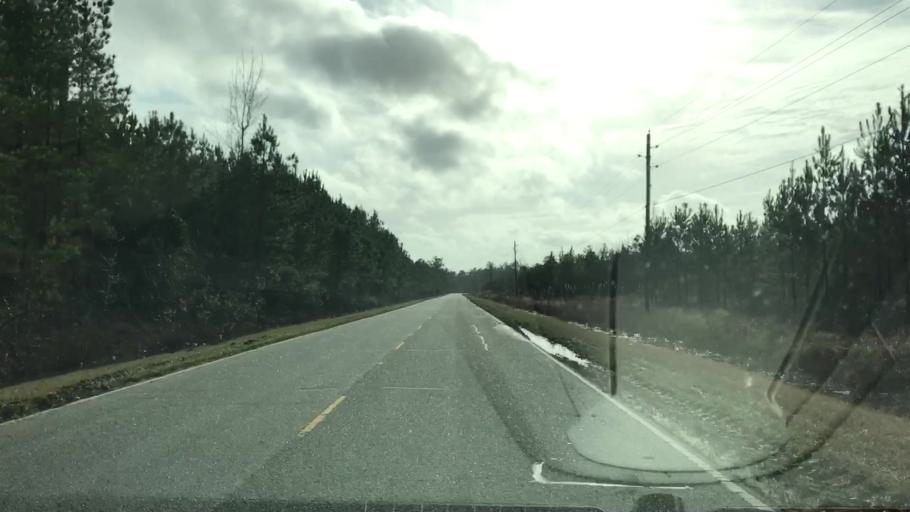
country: US
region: South Carolina
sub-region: Williamsburg County
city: Andrews
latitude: 33.4124
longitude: -79.6066
